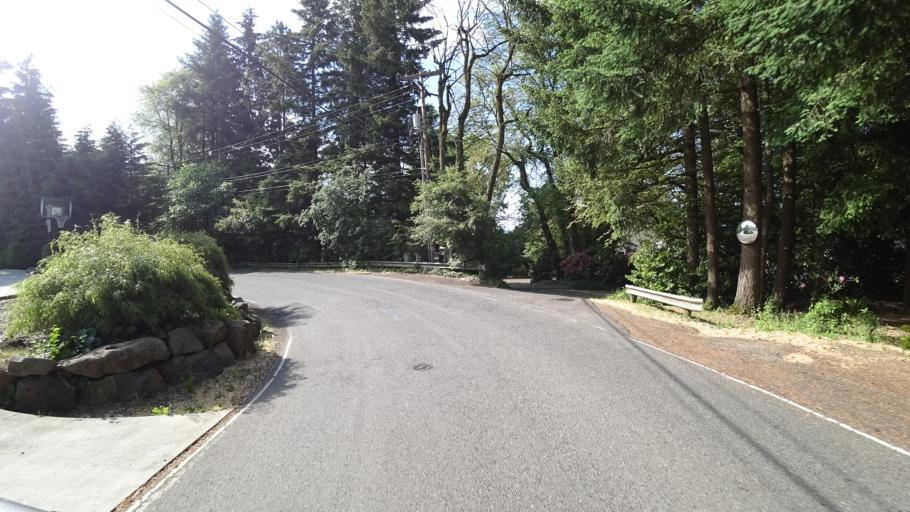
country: US
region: Oregon
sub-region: Washington County
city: West Slope
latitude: 45.5072
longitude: -122.7365
